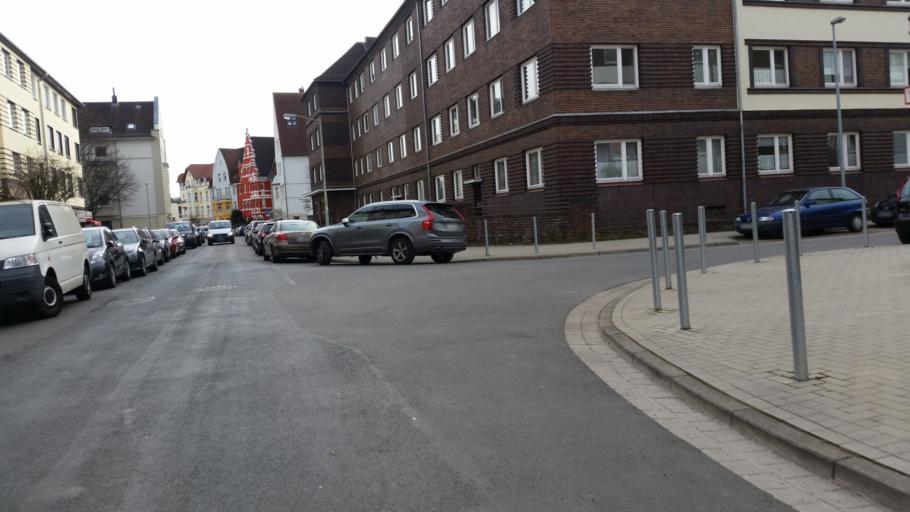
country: DE
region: Lower Saxony
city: Hannover
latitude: 52.4013
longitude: 9.7780
